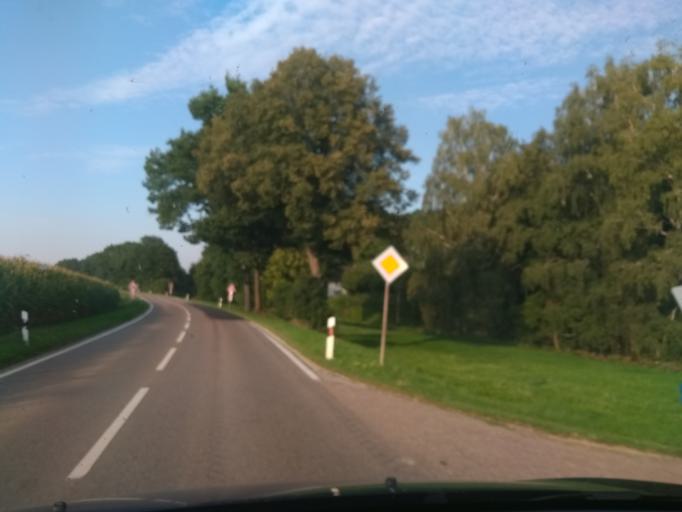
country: DE
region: Bavaria
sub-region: Upper Bavaria
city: Schwabhausen
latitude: 48.3143
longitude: 11.3872
